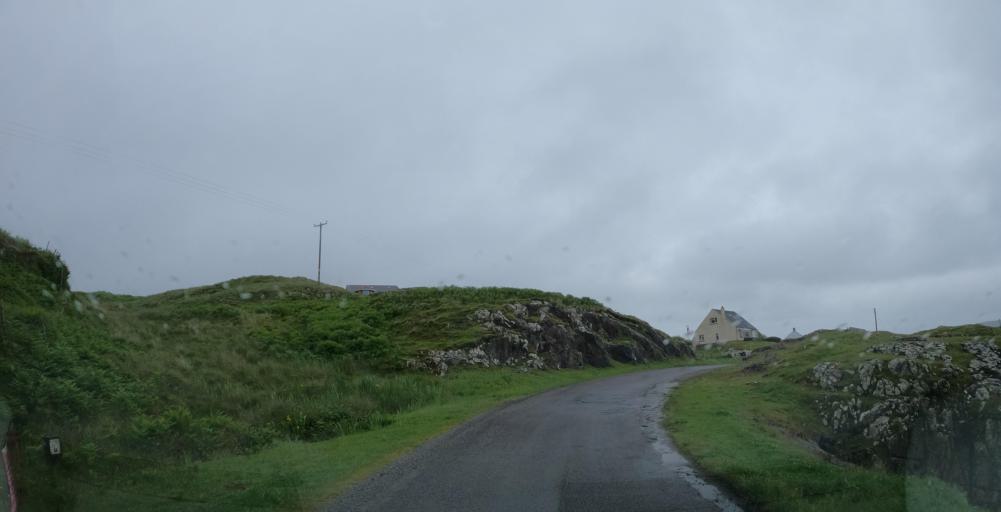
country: GB
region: Scotland
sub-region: Eilean Siar
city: Barra
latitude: 56.9721
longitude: -7.4247
